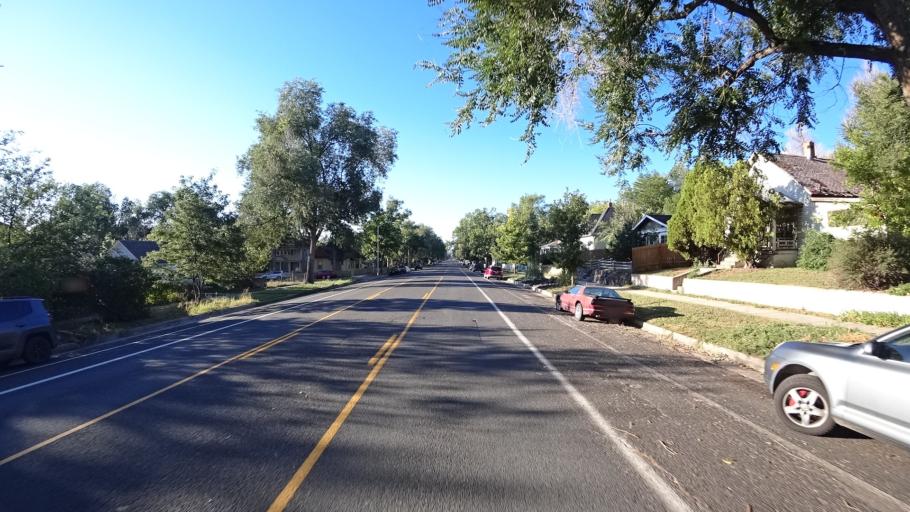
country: US
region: Colorado
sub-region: El Paso County
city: Colorado Springs
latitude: 38.8440
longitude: -104.8324
